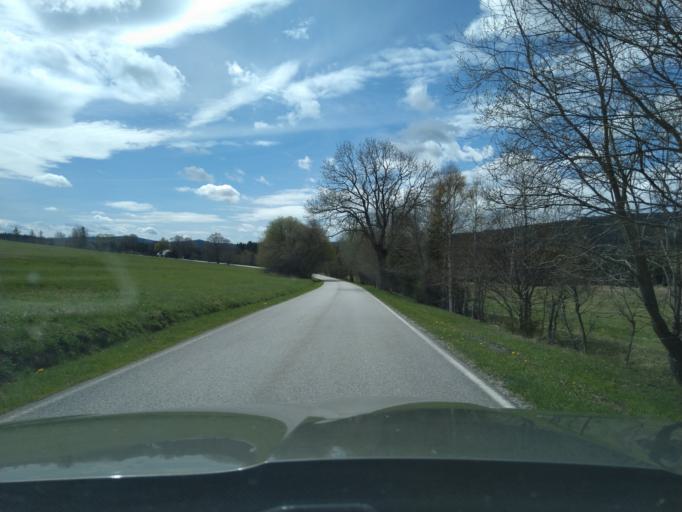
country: CZ
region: Jihocesky
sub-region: Okres Prachatice
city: Borova Lada
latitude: 49.0325
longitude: 13.6653
